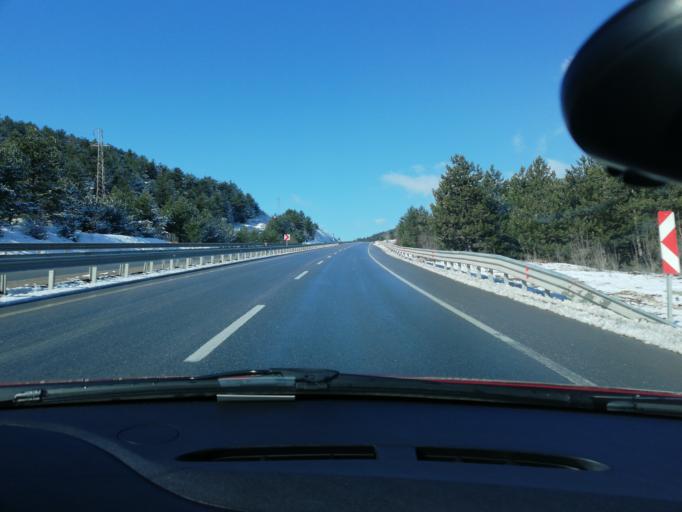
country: TR
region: Kastamonu
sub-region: Cide
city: Kastamonu
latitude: 41.3602
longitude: 33.7039
